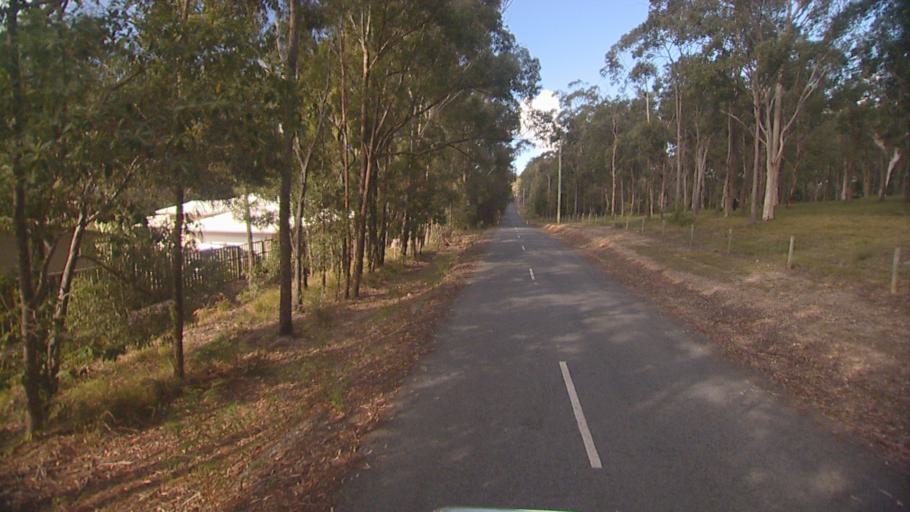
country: AU
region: Queensland
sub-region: Redland
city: Redland Bay
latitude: -27.6533
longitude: 153.2575
